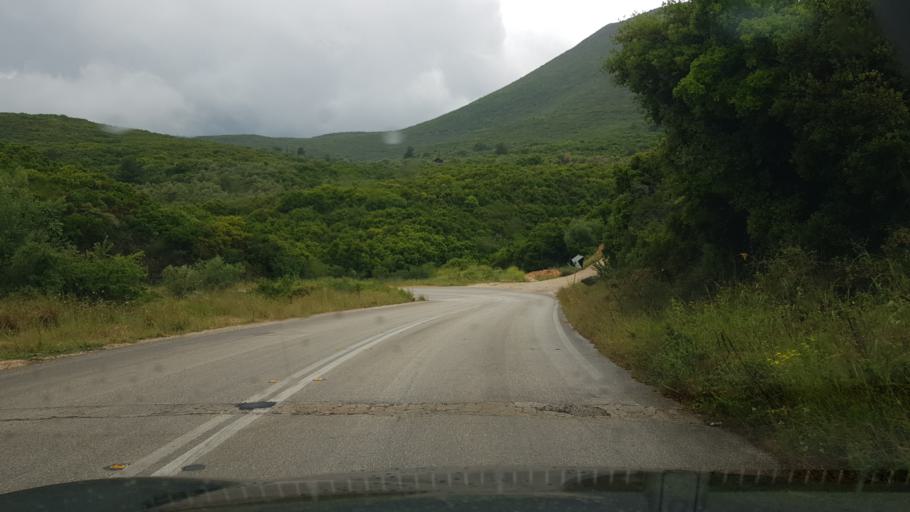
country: GR
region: Ionian Islands
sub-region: Lefkada
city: Nidri
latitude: 38.6494
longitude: 20.6771
